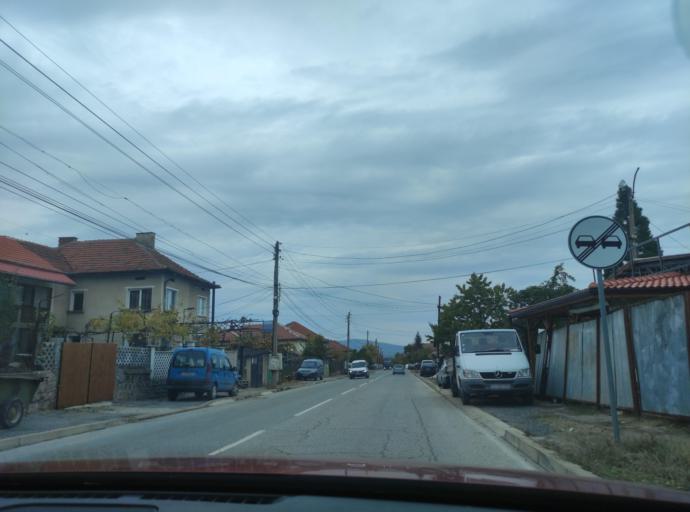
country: BG
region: Montana
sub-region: Obshtina Berkovitsa
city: Berkovitsa
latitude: 43.2057
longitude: 23.1601
